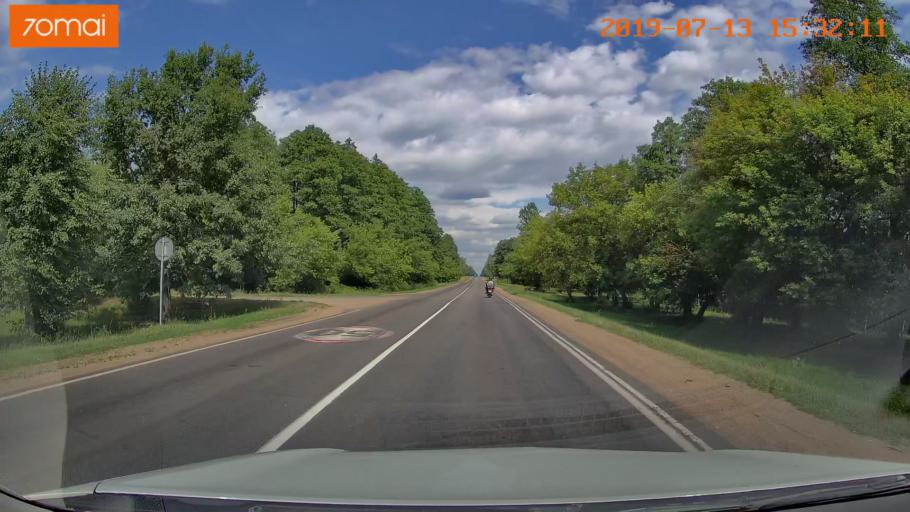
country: BY
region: Mogilev
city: Babruysk
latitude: 53.1151
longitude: 29.1157
